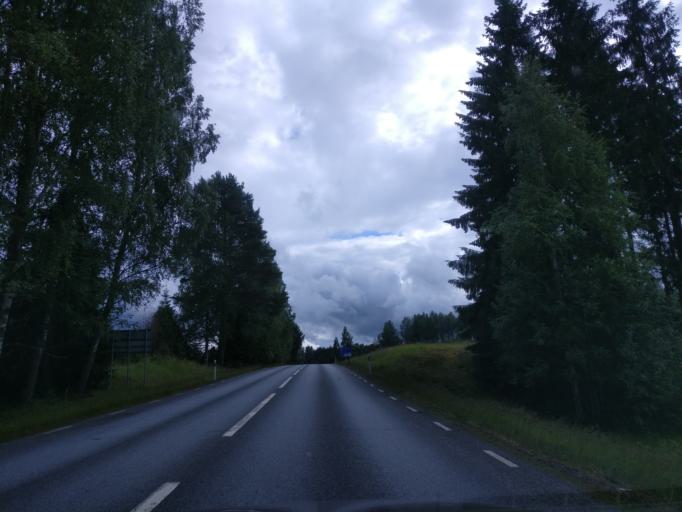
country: SE
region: Vaermland
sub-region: Hagfors Kommun
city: Hagfors
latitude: 59.9724
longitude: 13.5640
